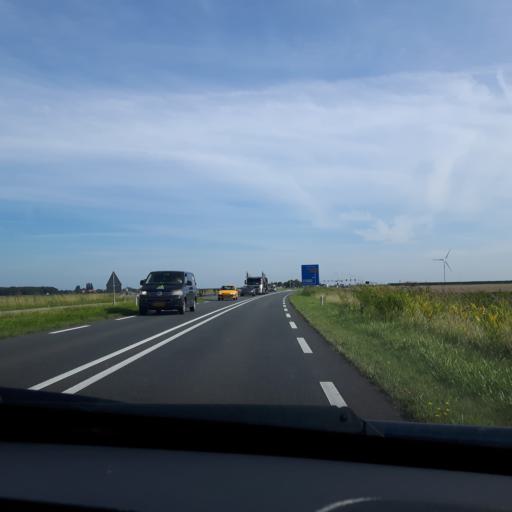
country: NL
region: Zeeland
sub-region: Gemeente Goes
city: Goes
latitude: 51.5807
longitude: 3.8510
